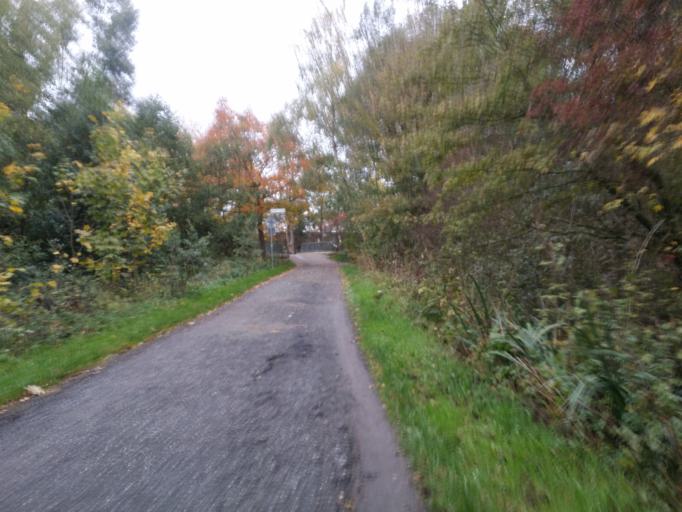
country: DE
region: Lower Saxony
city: Stuhr
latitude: 53.0458
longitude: 8.7461
